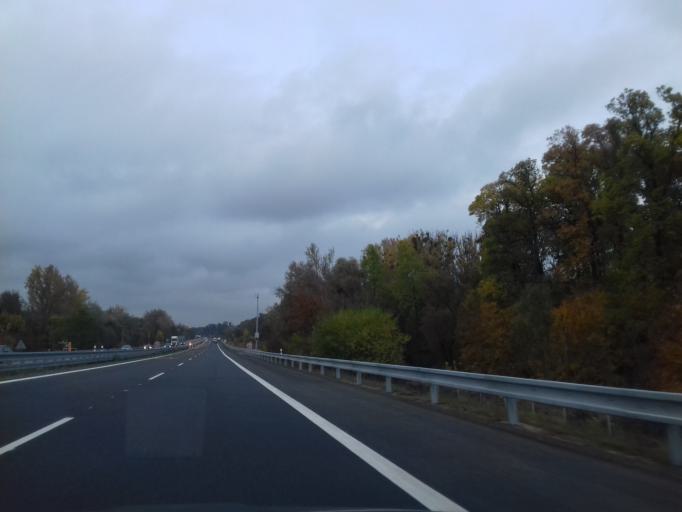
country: CZ
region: South Moravian
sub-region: Okres Breclav
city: Lanzhot
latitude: 48.6922
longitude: 16.9875
